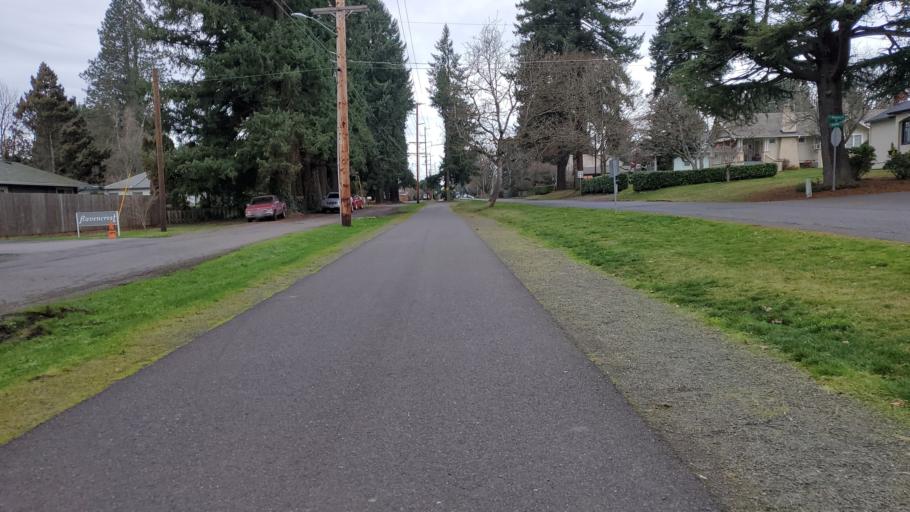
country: US
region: Oregon
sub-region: Clackamas County
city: Jennings Lodge
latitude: 45.3869
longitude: -122.6064
